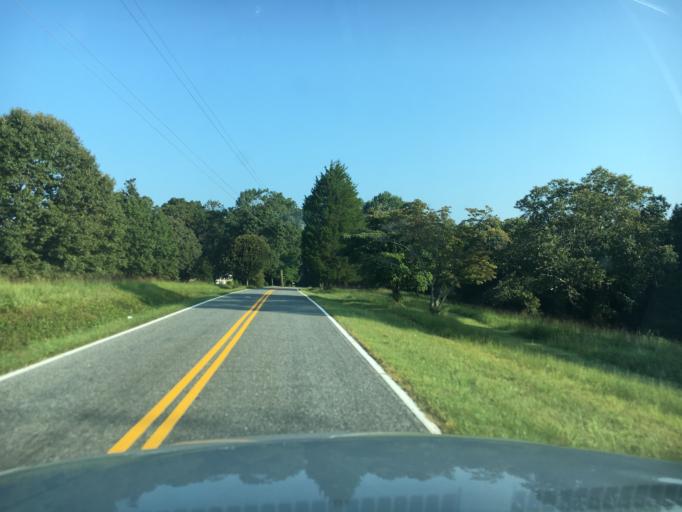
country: US
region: North Carolina
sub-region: Polk County
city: Columbus
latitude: 35.2367
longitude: -82.0524
